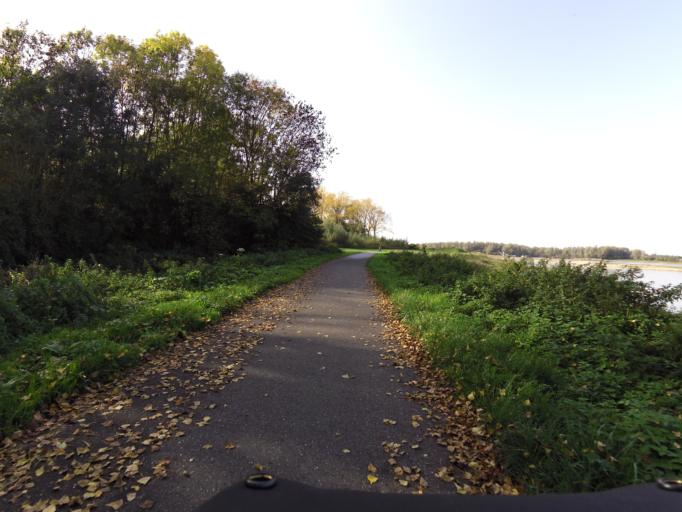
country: NL
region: Gelderland
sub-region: Gemeente Groesbeek
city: Berg en Dal
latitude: 51.8777
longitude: 5.9191
